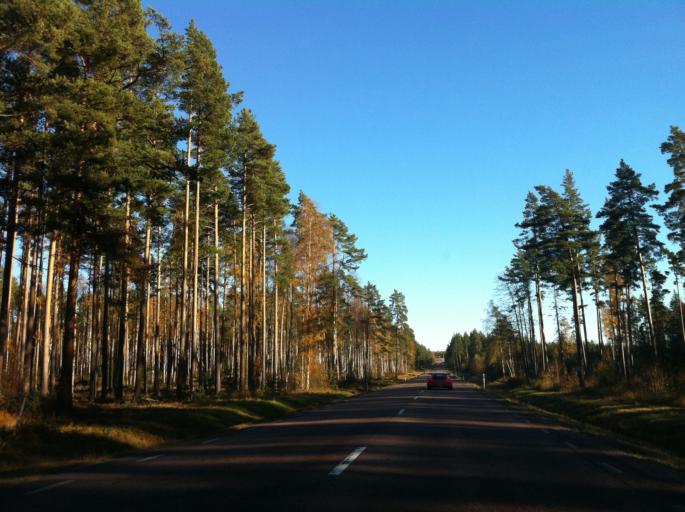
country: SE
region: Dalarna
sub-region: Leksand Municipality
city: Siljansnas
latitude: 60.9292
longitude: 14.7961
